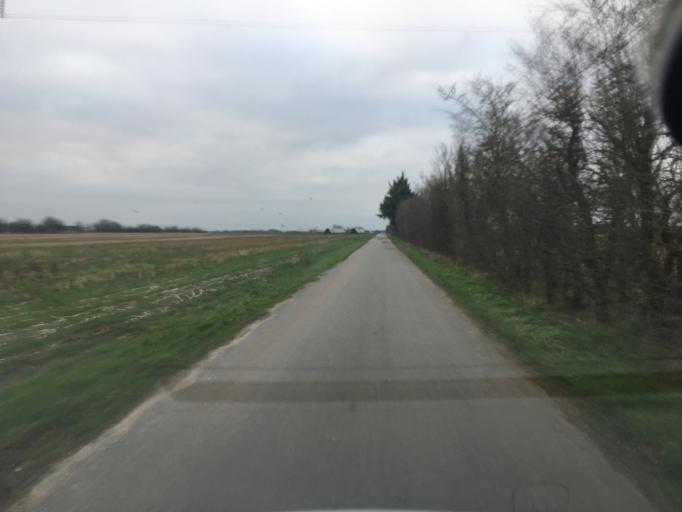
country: DK
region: South Denmark
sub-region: Tonder Kommune
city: Logumkloster
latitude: 55.0518
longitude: 9.0452
